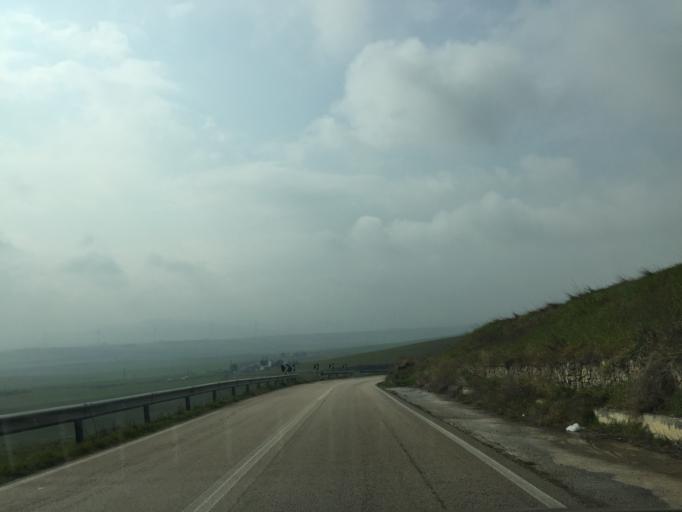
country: IT
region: Apulia
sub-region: Provincia di Foggia
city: Troia
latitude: 41.3657
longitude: 15.3264
